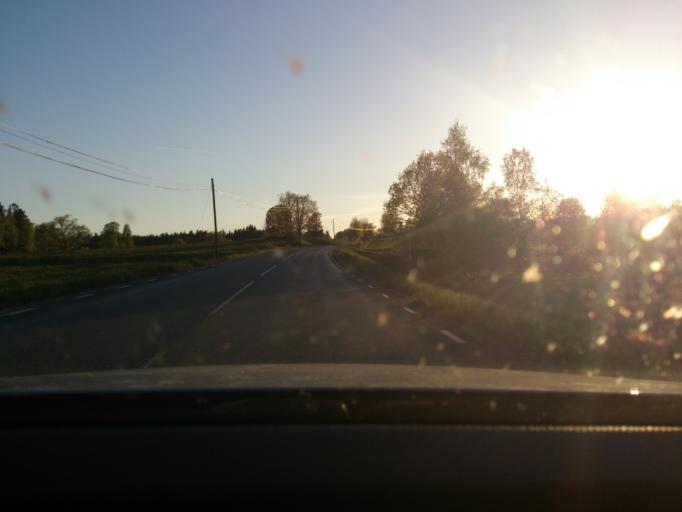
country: SE
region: Kronoberg
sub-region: Alvesta Kommun
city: Moheda
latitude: 56.9844
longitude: 14.6204
